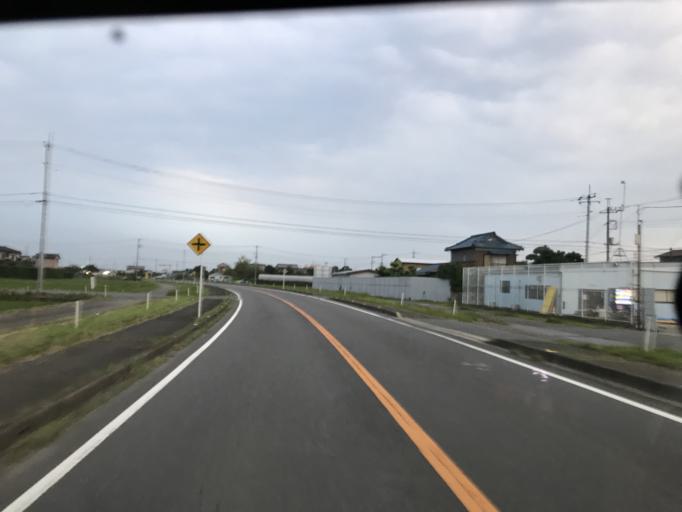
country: JP
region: Ibaraki
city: Ryugasaki
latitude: 35.8479
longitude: 140.1913
